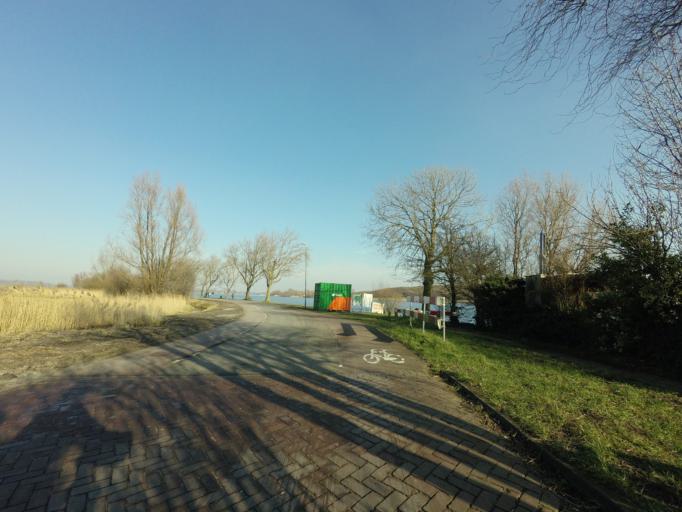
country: NL
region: North Holland
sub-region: Gemeente Haarlem
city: Haarlem
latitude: 52.4050
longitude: 4.6606
